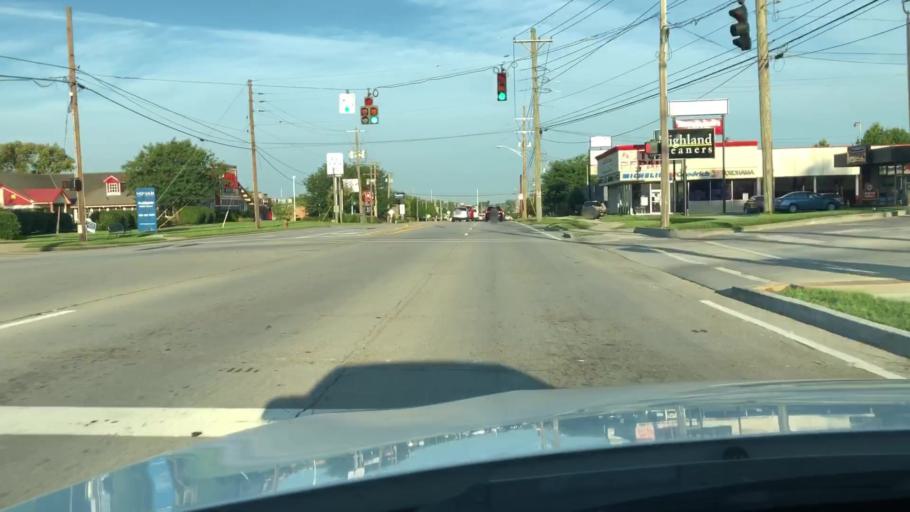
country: US
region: Kentucky
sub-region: Jefferson County
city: Saint Regis Park
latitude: 38.2197
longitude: -85.6220
